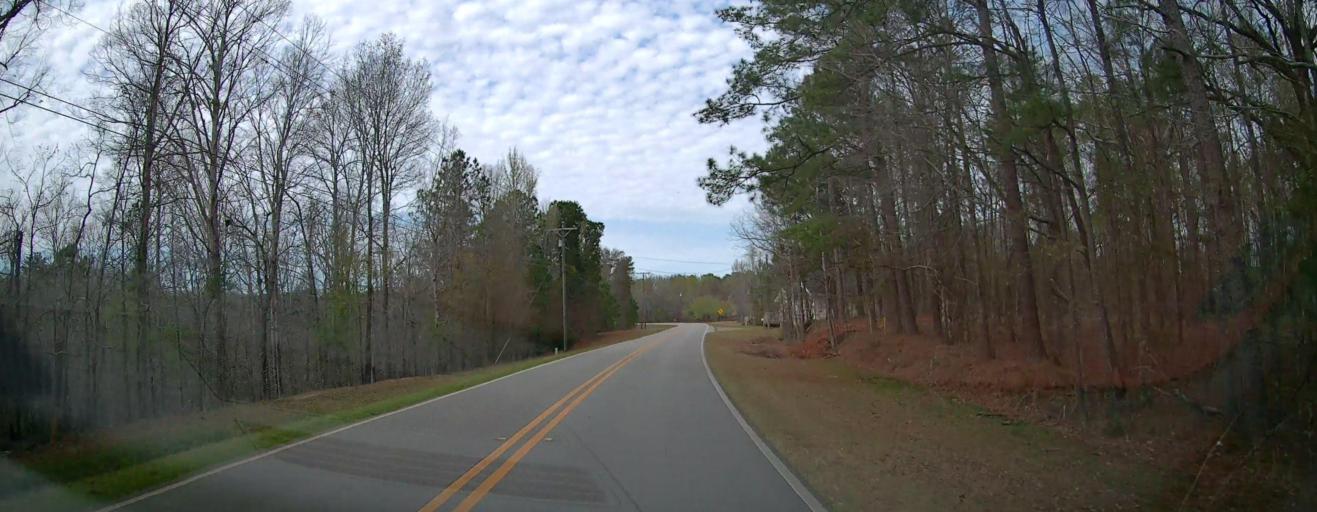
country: US
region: Georgia
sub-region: Bibb County
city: Macon
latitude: 32.9526
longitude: -83.6523
